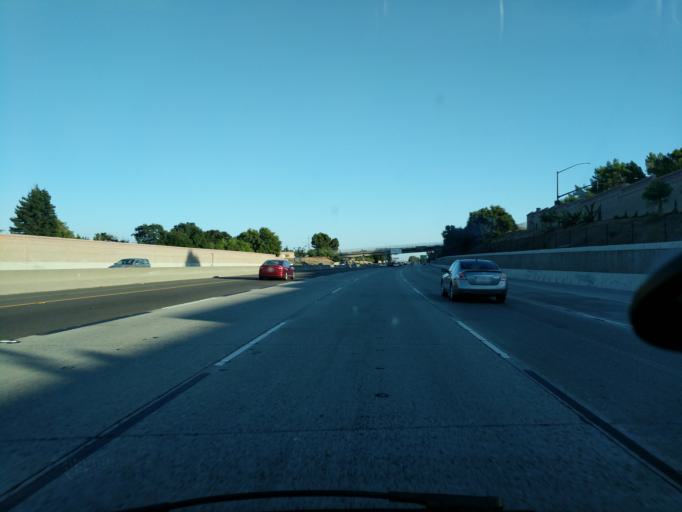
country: US
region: California
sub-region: Contra Costa County
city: San Ramon
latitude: 37.7949
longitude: -121.9846
